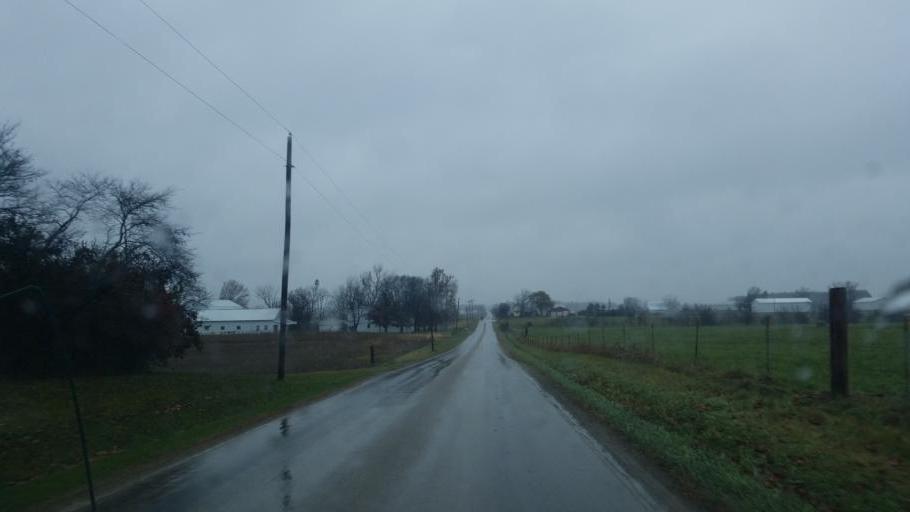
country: US
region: Indiana
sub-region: Adams County
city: Berne
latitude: 40.6260
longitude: -84.9356
